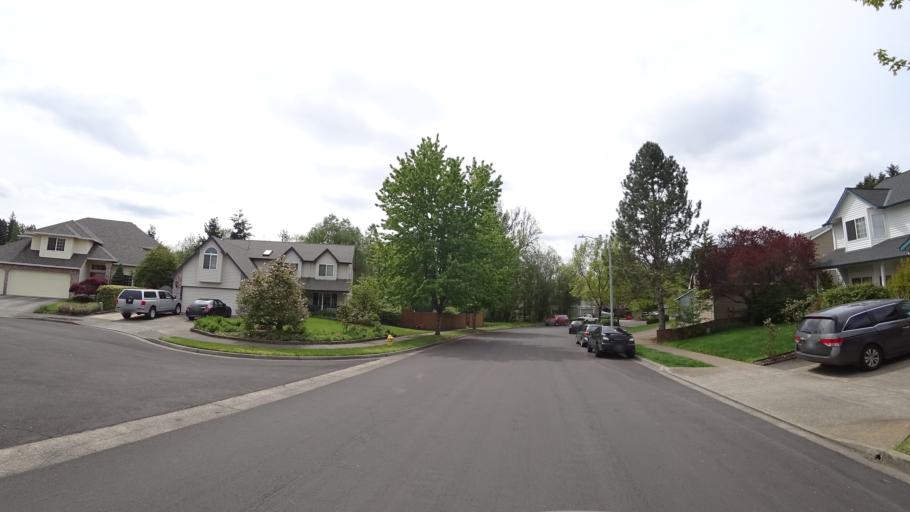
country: US
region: Oregon
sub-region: Washington County
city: Hillsboro
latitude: 45.5456
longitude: -122.9869
